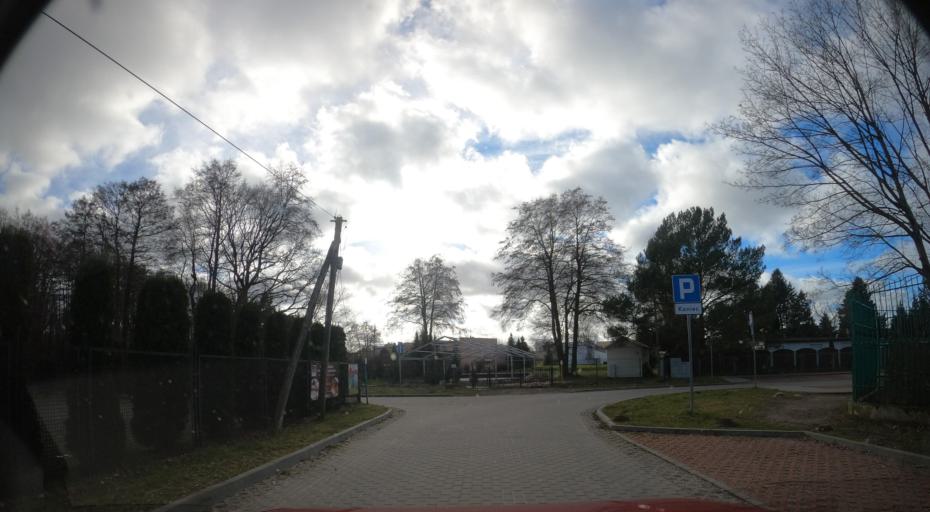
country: PL
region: West Pomeranian Voivodeship
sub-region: Koszalin
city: Koszalin
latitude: 54.3085
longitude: 16.2014
